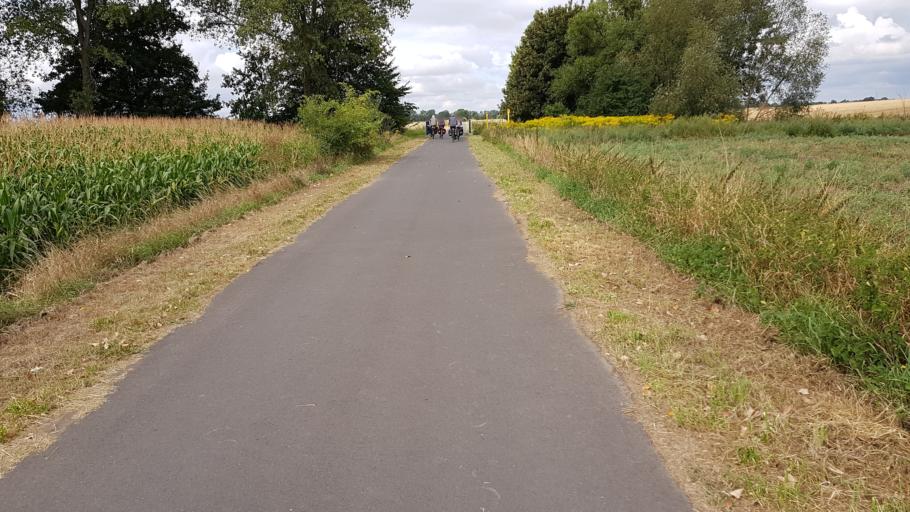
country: PL
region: West Pomeranian Voivodeship
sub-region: Powiat pyrzycki
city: Pyrzyce
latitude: 53.1457
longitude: 14.9225
